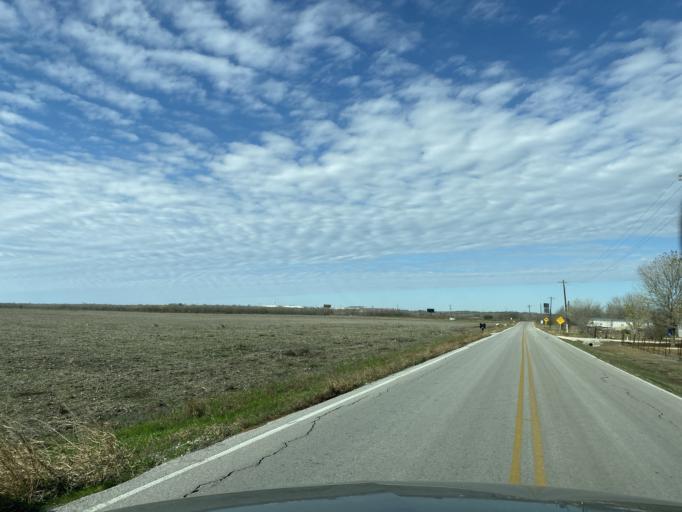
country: US
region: Texas
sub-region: Travis County
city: Onion Creek
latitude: 30.0863
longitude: -97.7053
